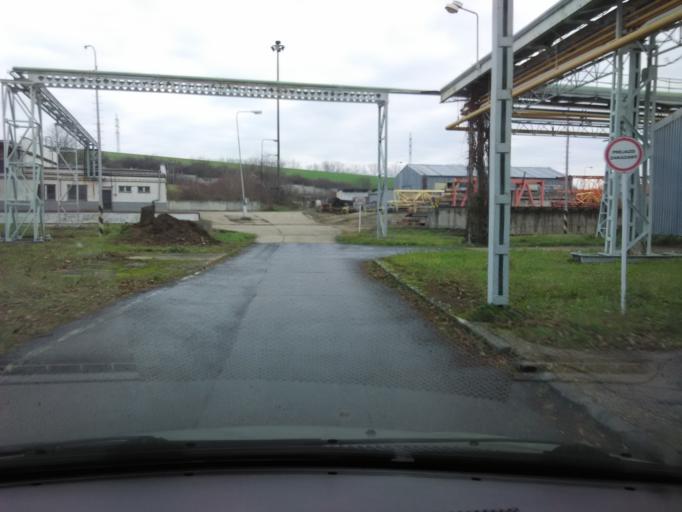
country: SK
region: Nitriansky
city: Tlmace
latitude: 48.2923
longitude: 18.5452
